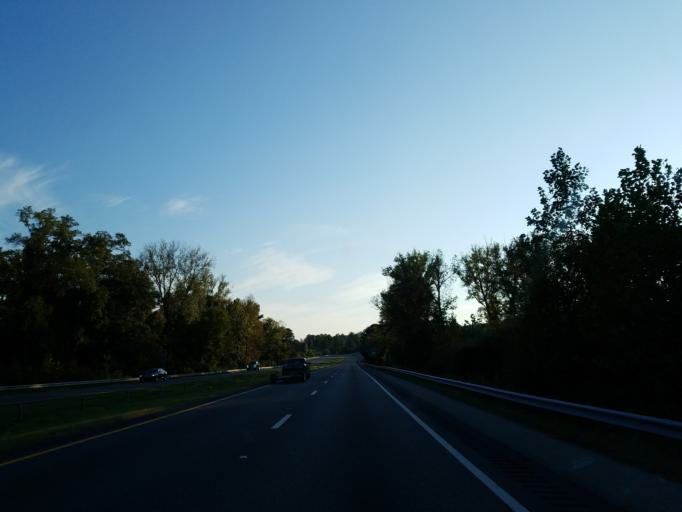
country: US
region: South Carolina
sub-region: Cherokee County
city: East Gaffney
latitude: 35.1149
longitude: -81.5801
